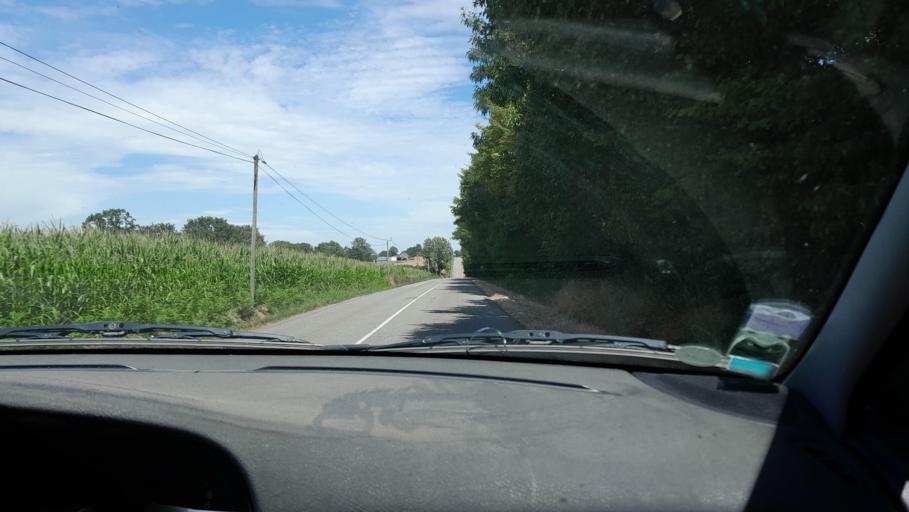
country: FR
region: Brittany
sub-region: Departement d'Ille-et-Vilaine
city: Le Pertre
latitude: 47.9676
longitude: -1.0418
